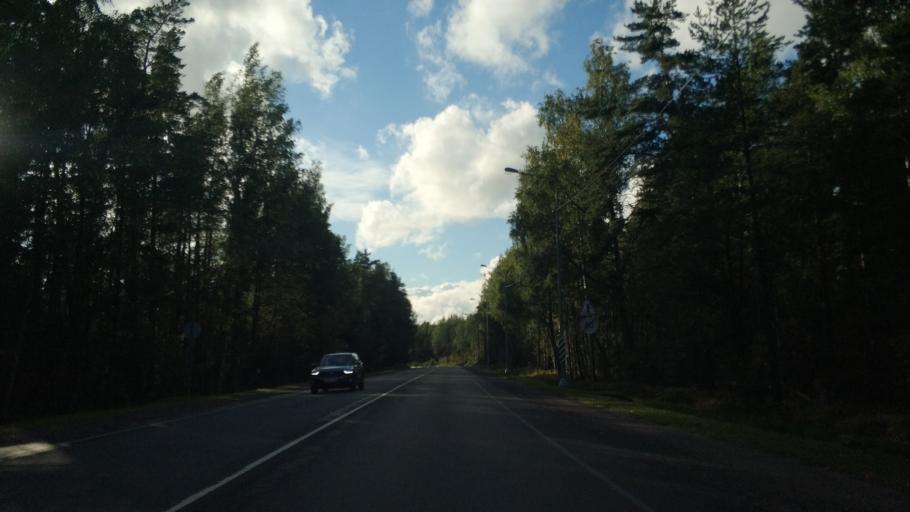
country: RU
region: Leningrad
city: Sapernoye
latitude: 60.7141
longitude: 30.0160
